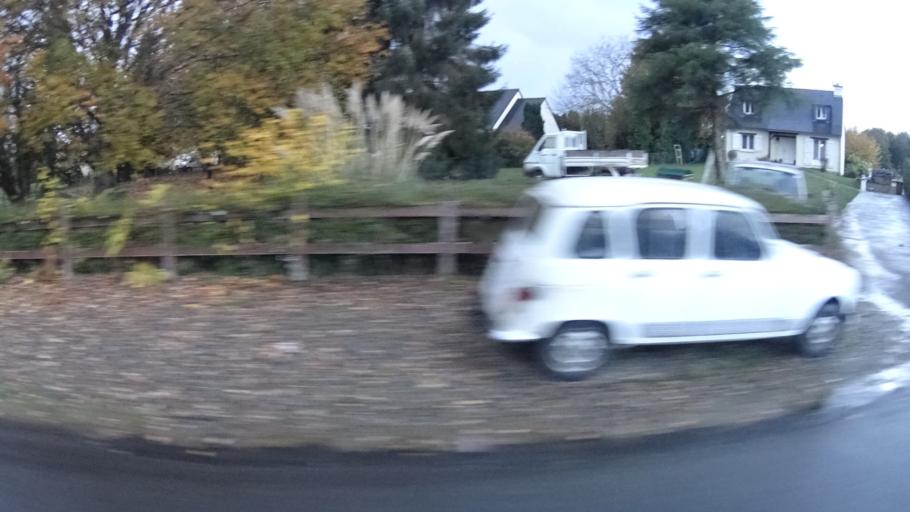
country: FR
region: Brittany
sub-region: Departement d'Ille-et-Vilaine
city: Sainte-Marie
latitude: 47.6901
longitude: -1.9988
